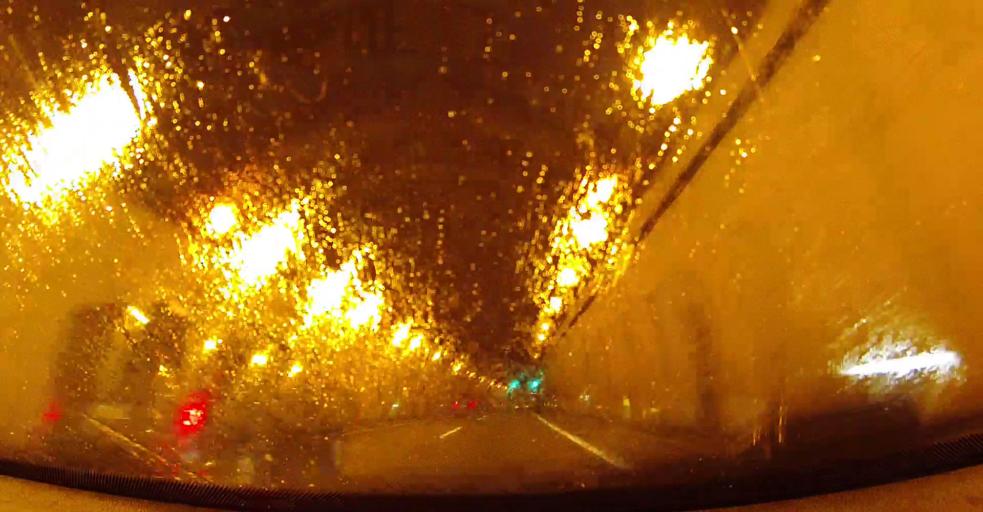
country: ES
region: Basque Country
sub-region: Provincia de Guipuzcoa
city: Getaria
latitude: 43.2813
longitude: -2.2078
